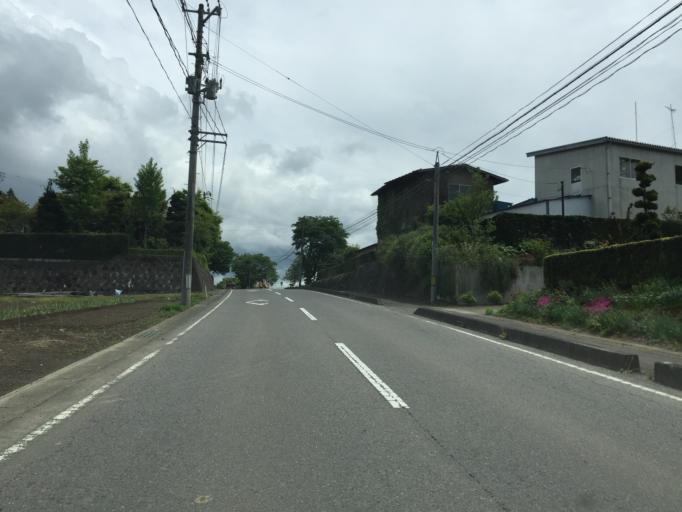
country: JP
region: Fukushima
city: Ishikawa
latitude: 37.1132
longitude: 140.3270
